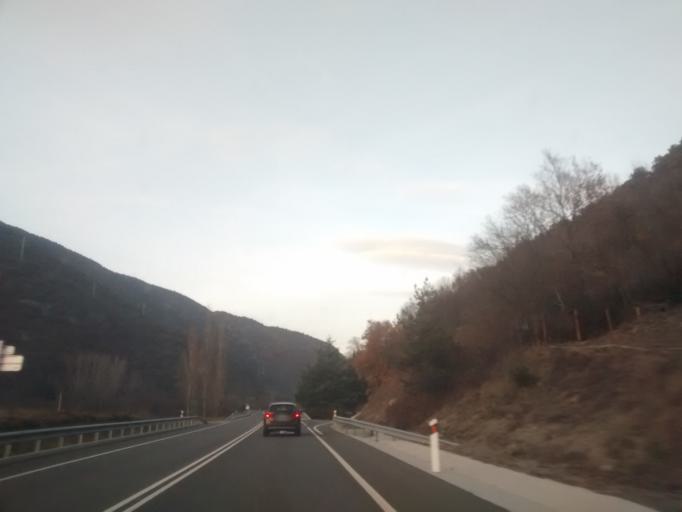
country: ES
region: Catalonia
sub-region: Provincia de Lleida
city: la Seu d'Urgell
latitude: 42.3837
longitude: 1.4599
